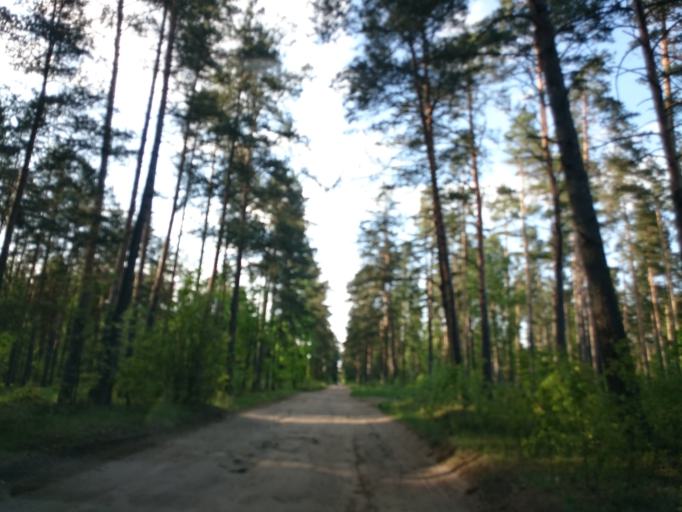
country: LV
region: Stopini
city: Ulbroka
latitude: 56.9488
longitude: 24.2885
